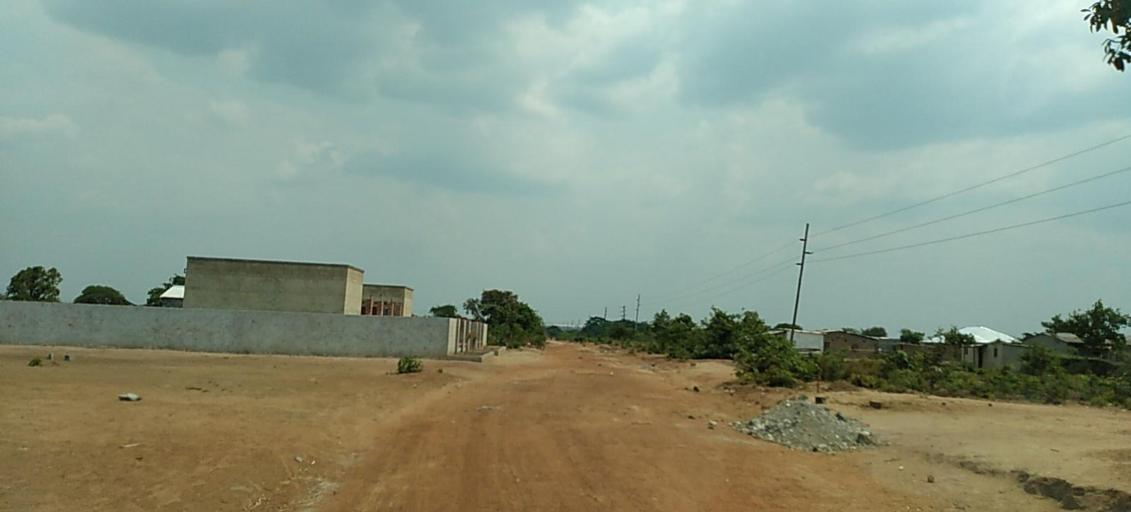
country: ZM
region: Copperbelt
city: Kalulushi
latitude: -12.8672
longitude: 28.0779
